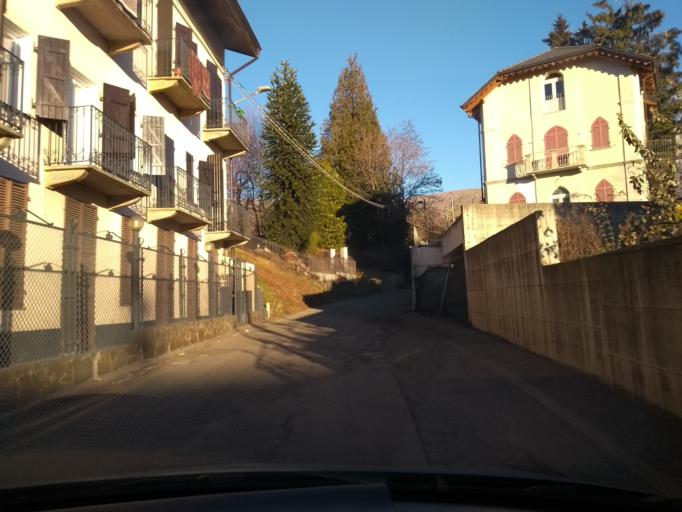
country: IT
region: Piedmont
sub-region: Provincia di Torino
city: Corio
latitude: 45.3143
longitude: 7.5301
